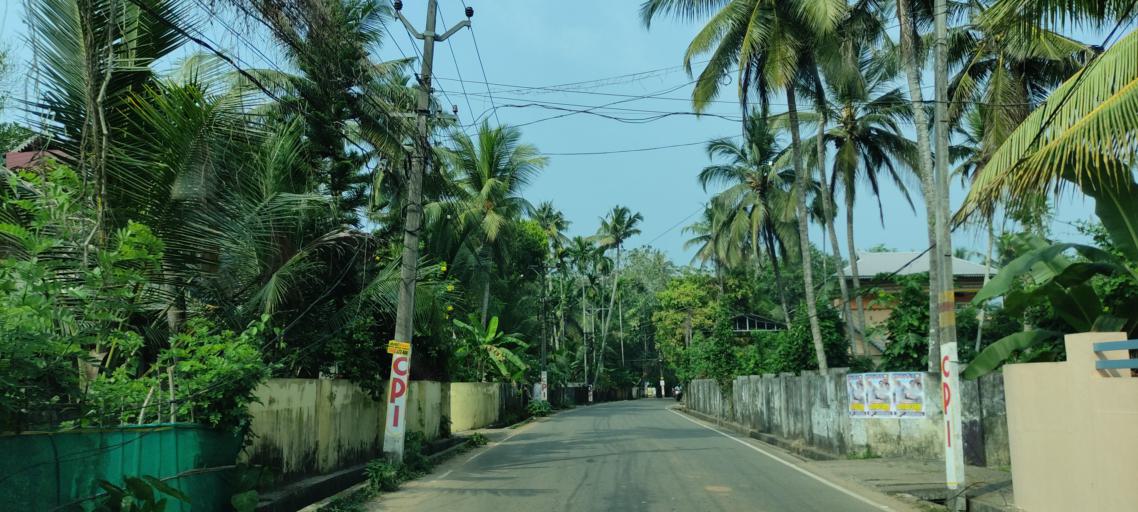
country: IN
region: Kerala
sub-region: Kottayam
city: Vaikam
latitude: 9.7522
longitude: 76.4023
